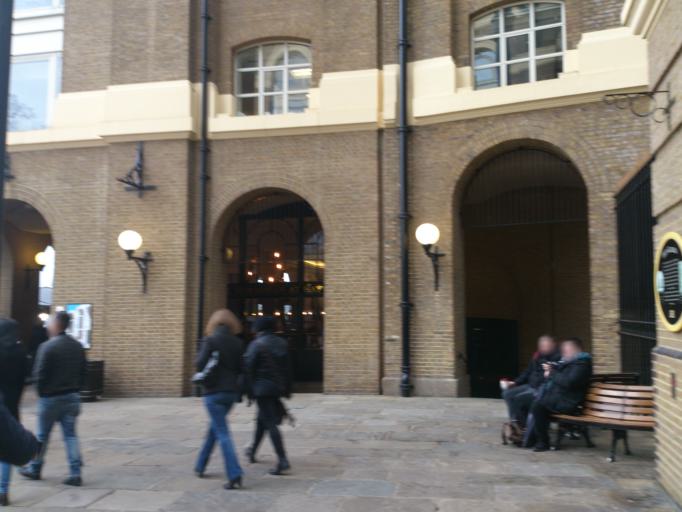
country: GB
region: England
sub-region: Greater London
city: City of London
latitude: 51.5063
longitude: -0.0833
